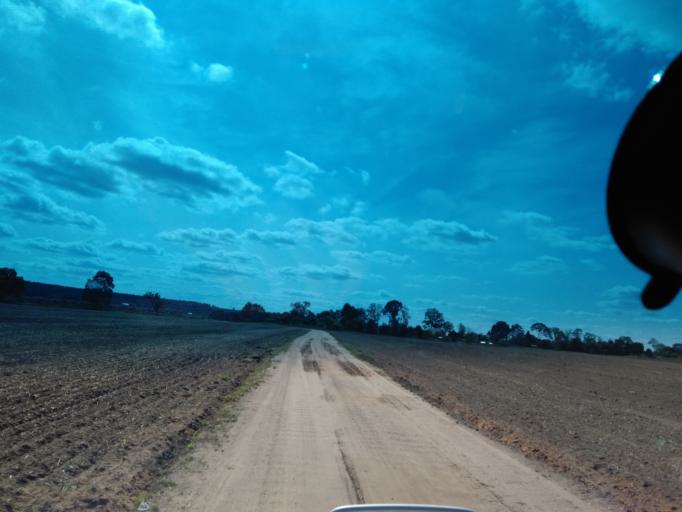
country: BY
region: Minsk
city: Stan'kava
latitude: 53.6376
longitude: 27.3085
